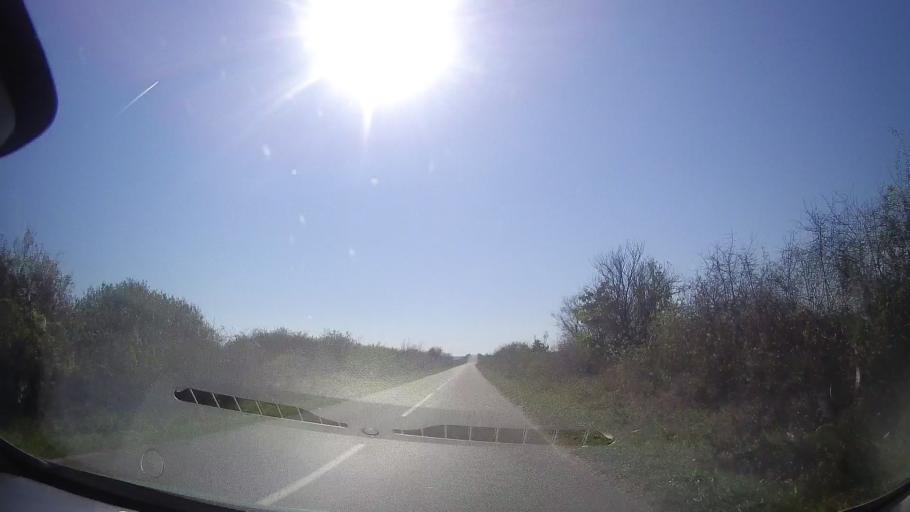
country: RO
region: Timis
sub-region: Comuna Bethausen
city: Bethausen
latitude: 45.8210
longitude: 21.9599
